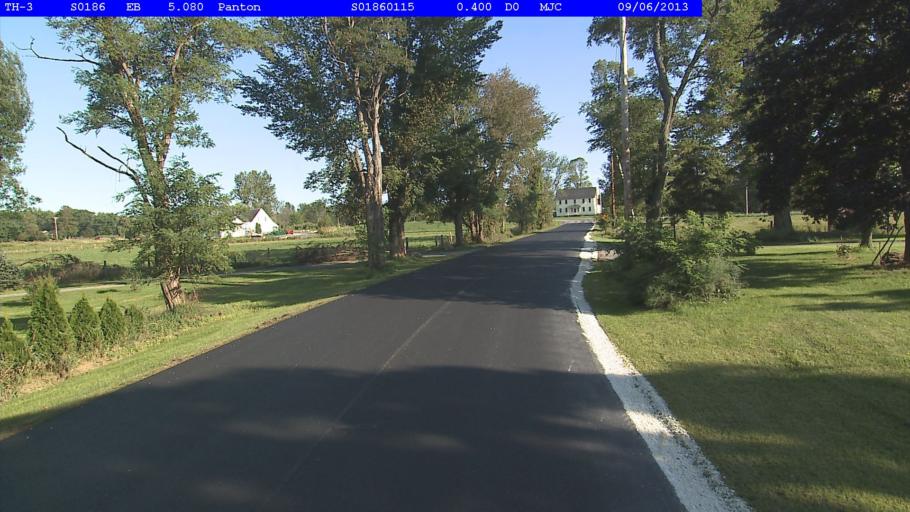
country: US
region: Vermont
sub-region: Addison County
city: Vergennes
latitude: 44.1597
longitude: -73.2865
